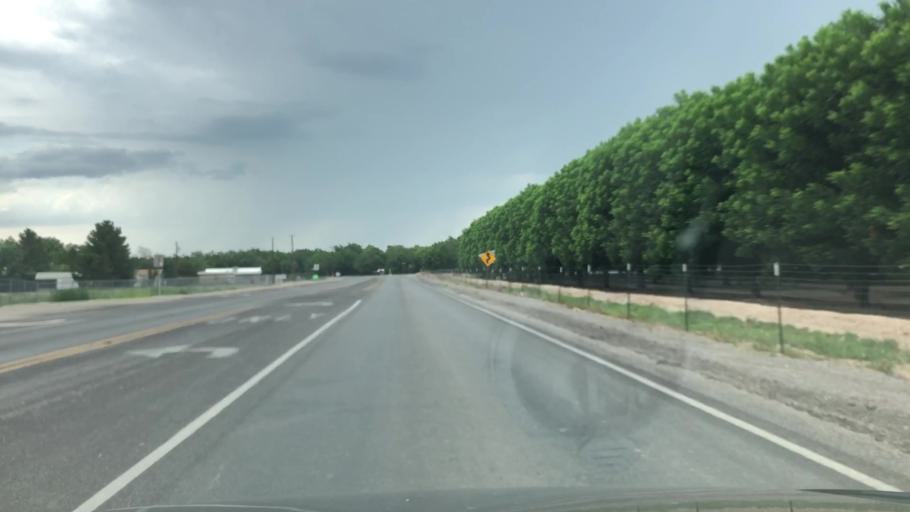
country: US
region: New Mexico
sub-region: Dona Ana County
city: La Union
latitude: 32.0003
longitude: -106.6564
